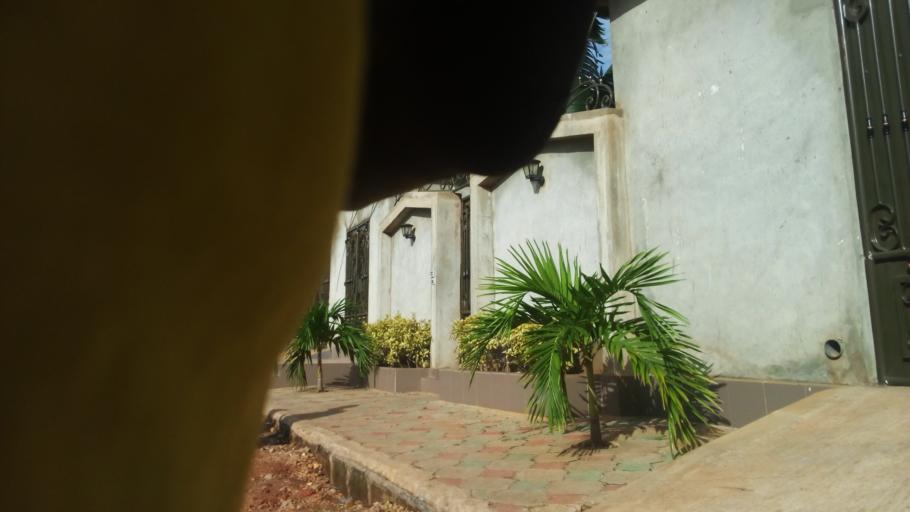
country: BJ
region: Atlantique
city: Abomey-Calavi
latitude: 6.4265
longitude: 2.3393
